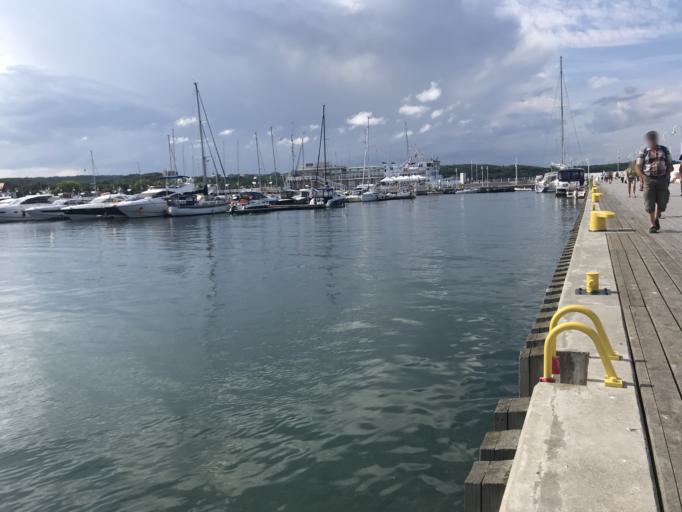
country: PL
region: Pomeranian Voivodeship
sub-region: Sopot
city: Sopot
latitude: 54.4473
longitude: 18.5792
